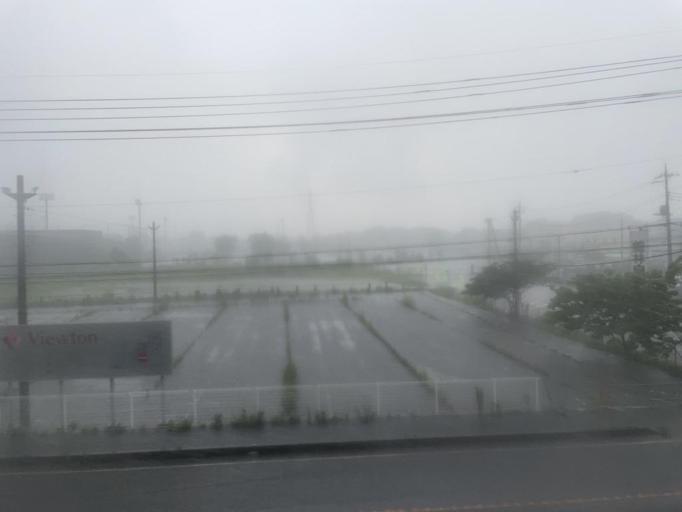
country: JP
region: Gunma
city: Tatebayashi
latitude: 36.2666
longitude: 139.5110
